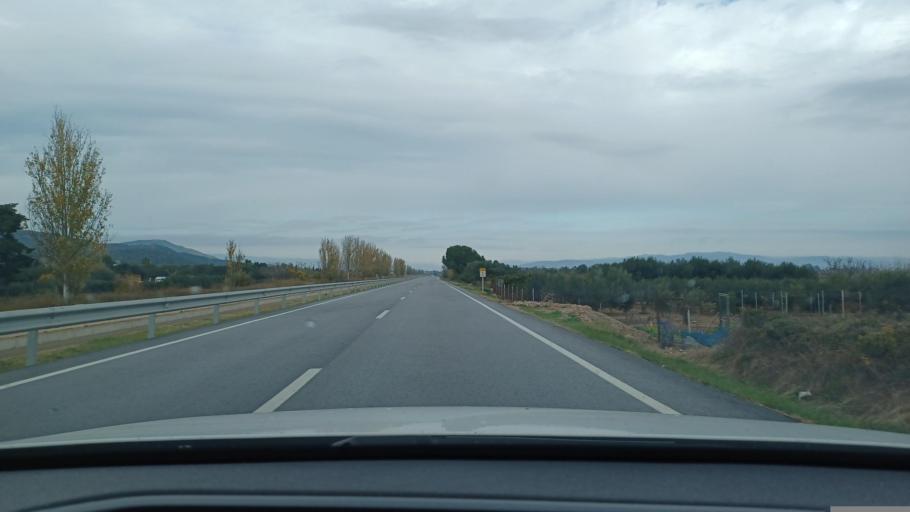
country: ES
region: Catalonia
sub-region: Provincia de Tarragona
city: Sant Carles de la Rapita
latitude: 40.6466
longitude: 0.5984
